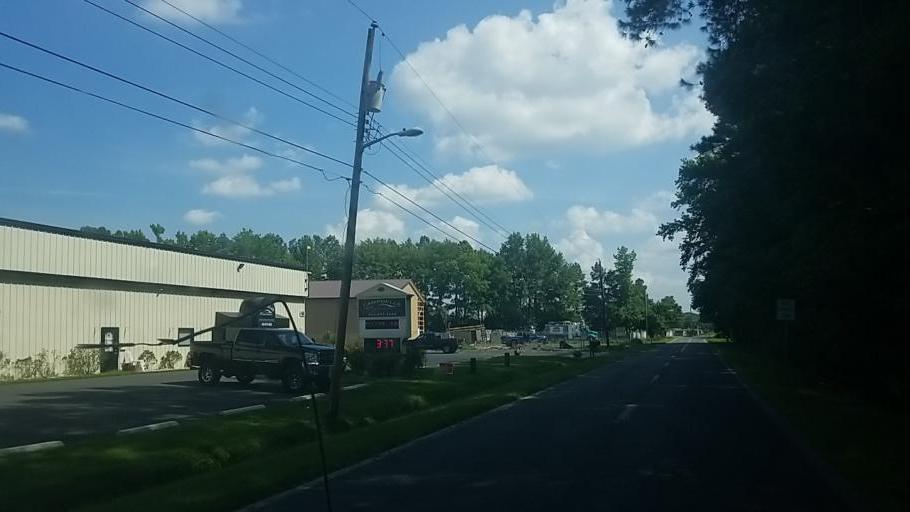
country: US
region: Maryland
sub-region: Wicomico County
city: Fruitland
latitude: 38.3106
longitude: -75.6321
